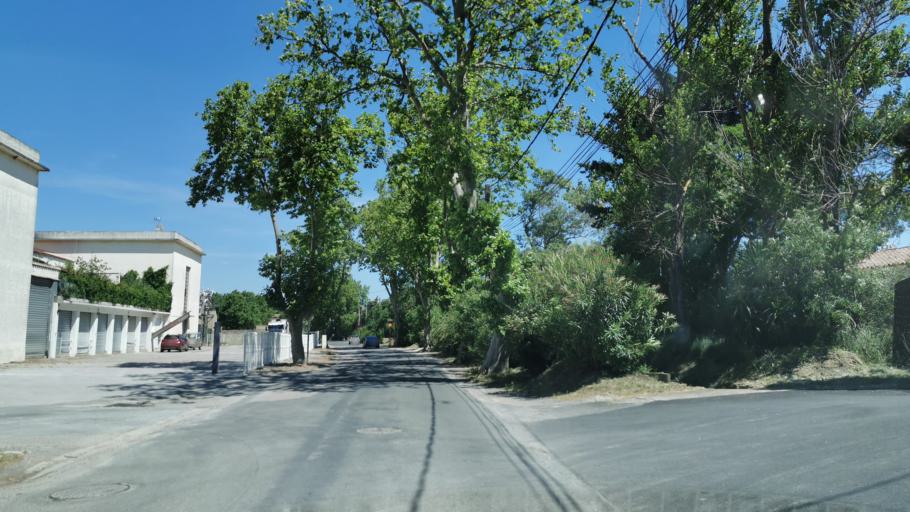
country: FR
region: Languedoc-Roussillon
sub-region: Departement de l'Aude
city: Canet
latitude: 43.2225
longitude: 2.8462
